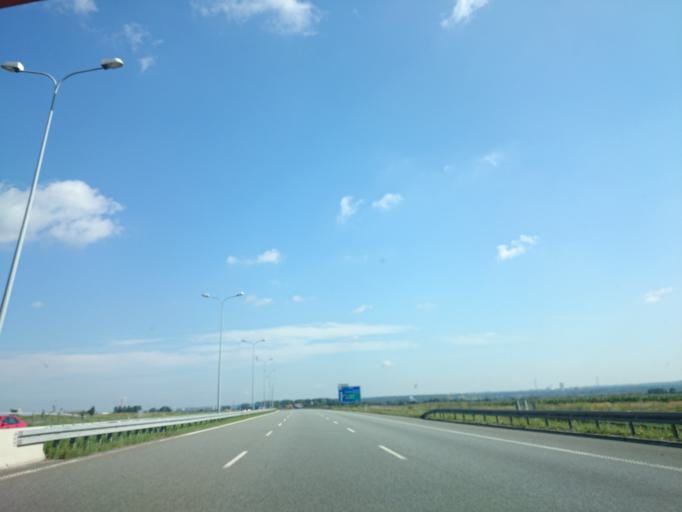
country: PL
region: Silesian Voivodeship
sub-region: Powiat gliwicki
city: Gieraltowice
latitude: 50.2417
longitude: 18.7107
